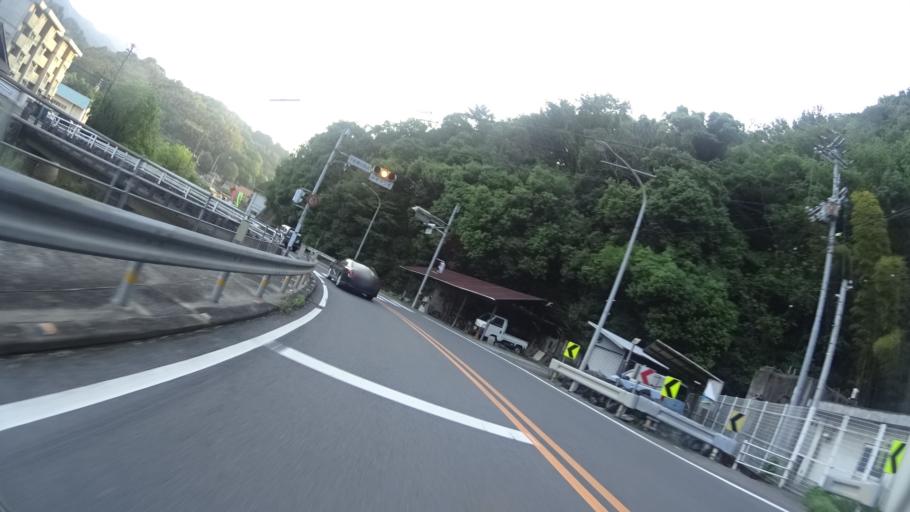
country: JP
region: Ehime
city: Kawanoecho
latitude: 33.9922
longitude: 133.6264
